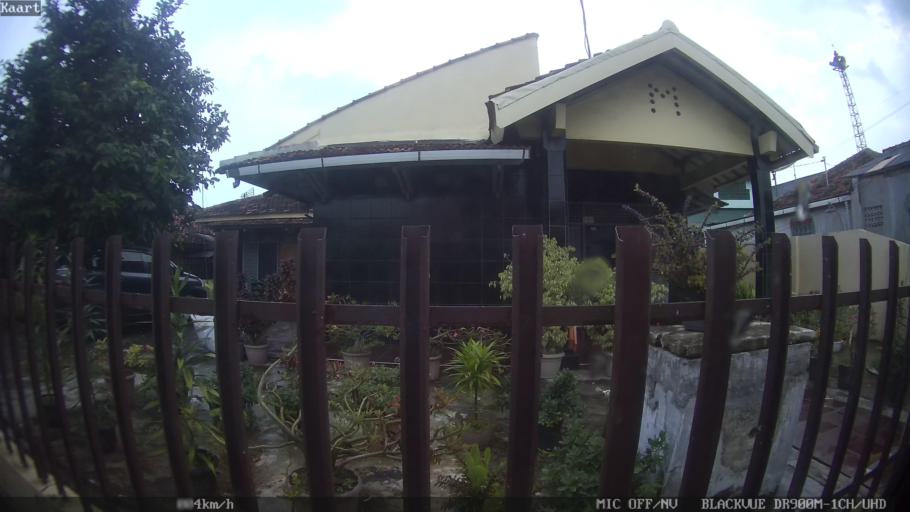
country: ID
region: Lampung
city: Bandarlampung
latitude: -5.4424
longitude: 105.2740
